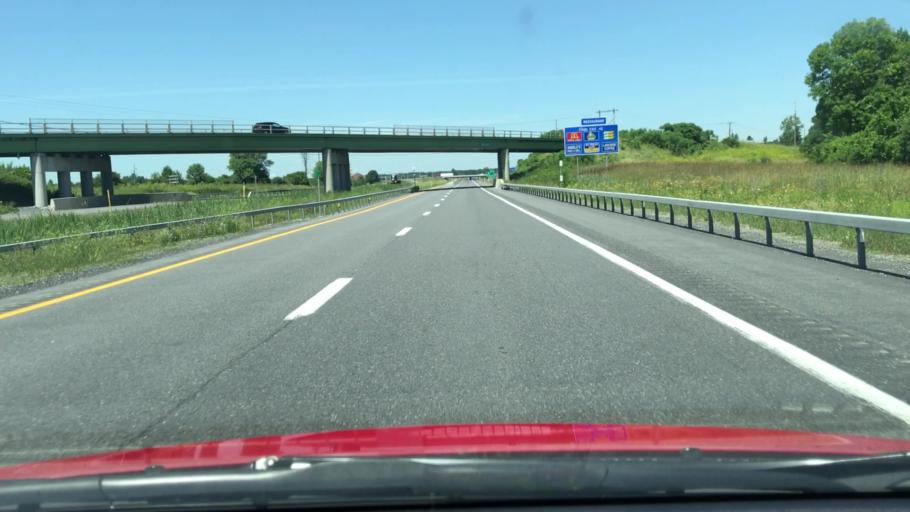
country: US
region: New York
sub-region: Clinton County
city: Champlain
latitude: 44.9722
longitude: -73.4522
